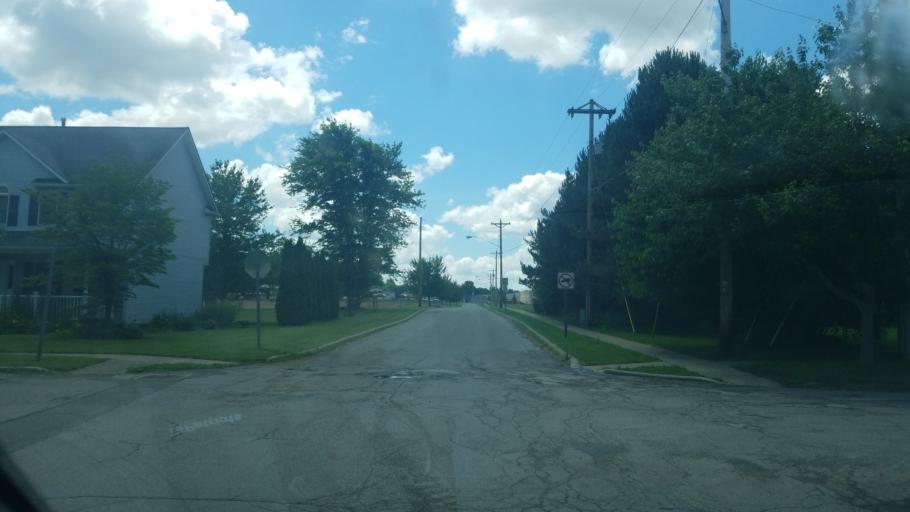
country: US
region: Ohio
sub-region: Huron County
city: New London
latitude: 41.0799
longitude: -82.3897
